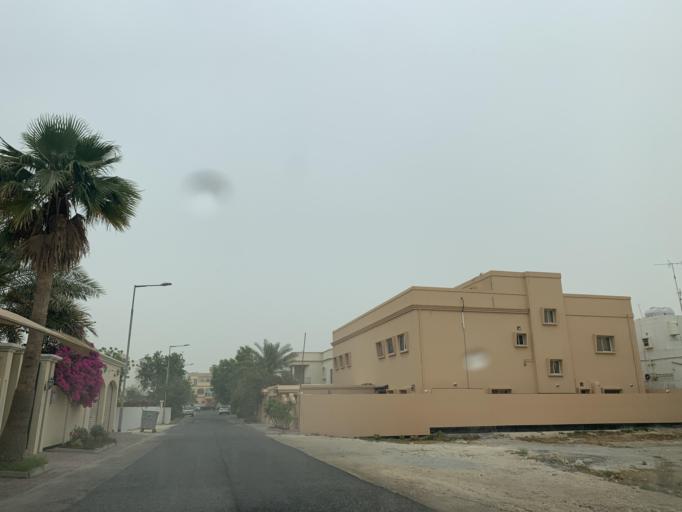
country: BH
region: Northern
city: Ar Rifa'
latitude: 26.1474
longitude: 50.5327
